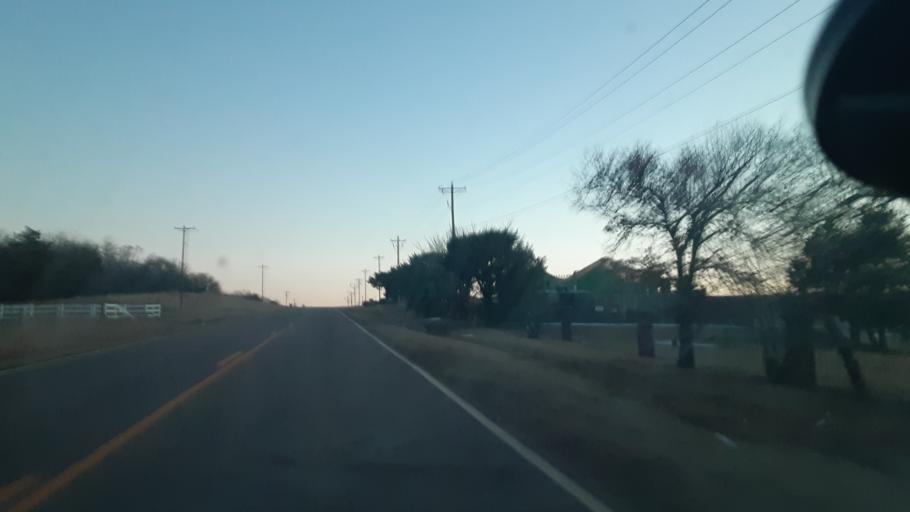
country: US
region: Oklahoma
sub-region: Oklahoma County
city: Edmond
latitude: 35.6881
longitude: -97.4251
